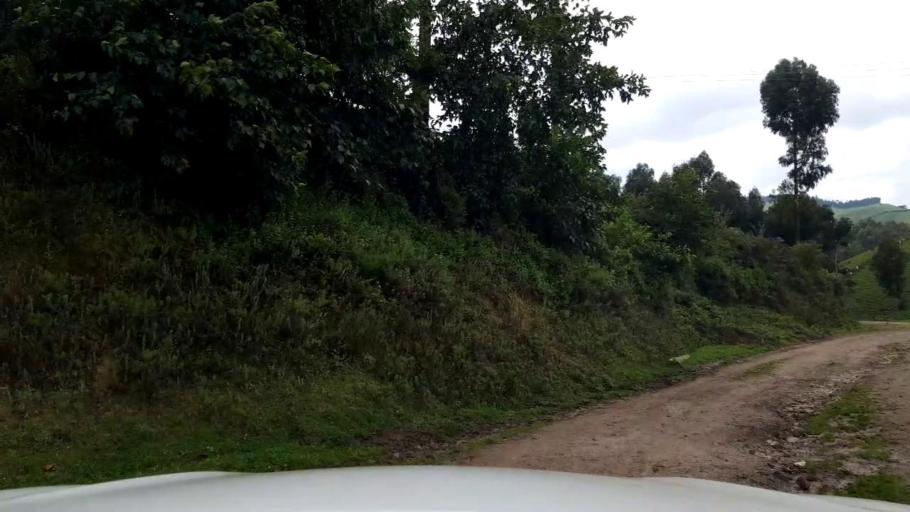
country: RW
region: Western Province
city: Gisenyi
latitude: -1.6835
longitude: 29.4178
